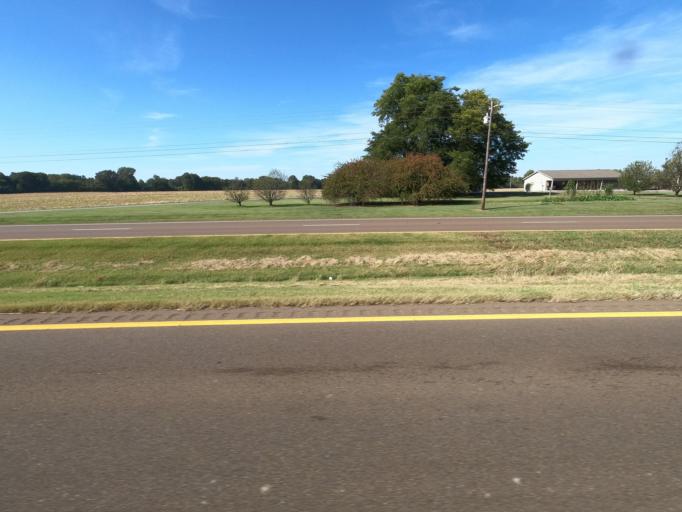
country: US
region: Tennessee
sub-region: Obion County
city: Englewood
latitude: 36.3885
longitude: -89.1035
